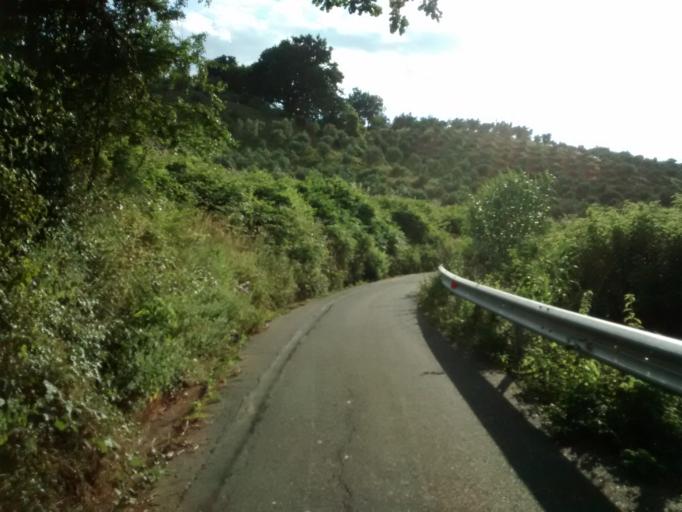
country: IT
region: Calabria
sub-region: Provincia di Catanzaro
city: Cortale
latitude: 38.8828
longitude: 16.4106
